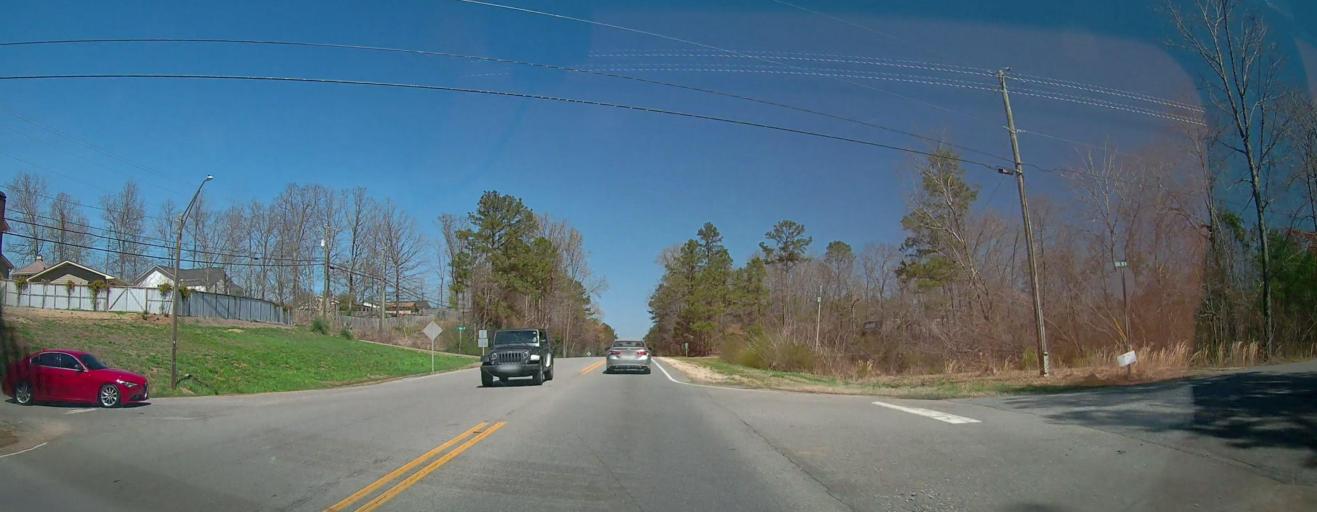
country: US
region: Alabama
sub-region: Etowah County
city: Southside
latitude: 33.8736
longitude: -86.0358
